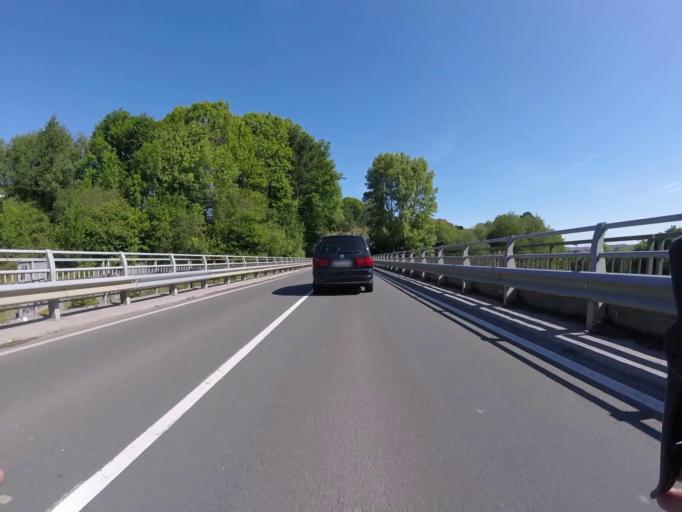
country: ES
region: Basque Country
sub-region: Provincia de Guipuzcoa
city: Irun
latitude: 43.3197
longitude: -1.8289
